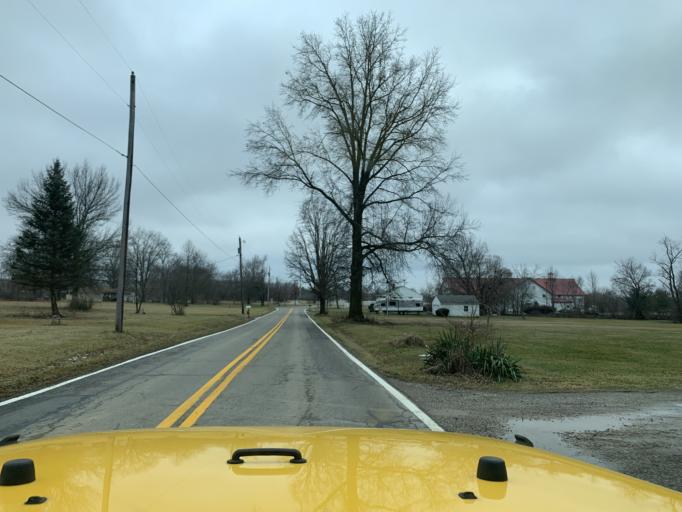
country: US
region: Ohio
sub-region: Franklin County
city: New Albany
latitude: 40.0942
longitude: -82.7932
